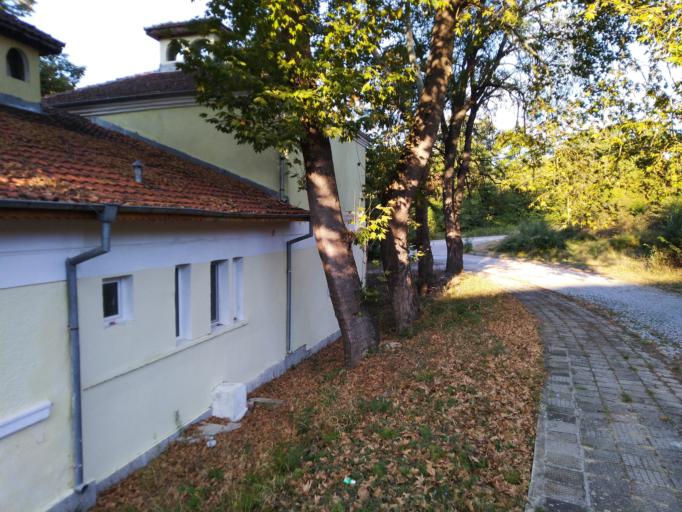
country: BG
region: Plovdiv
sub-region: Obshtina Khisarya
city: Khisarya
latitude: 42.5017
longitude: 24.7007
